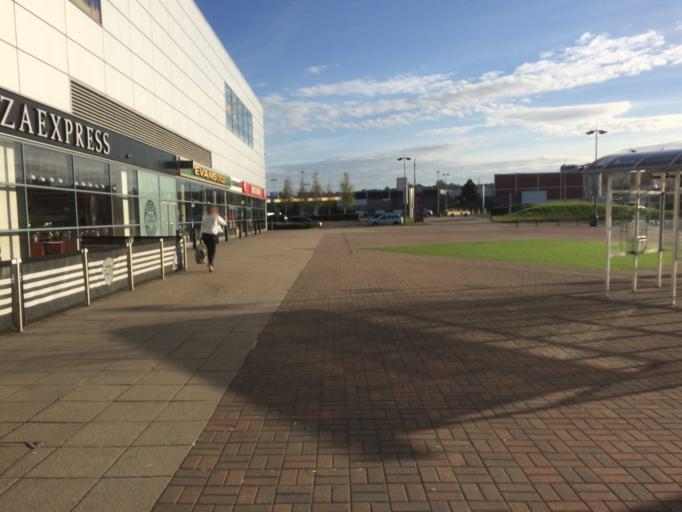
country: GB
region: England
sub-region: City and Borough of Wakefield
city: Castleford
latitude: 53.7101
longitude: -1.3404
